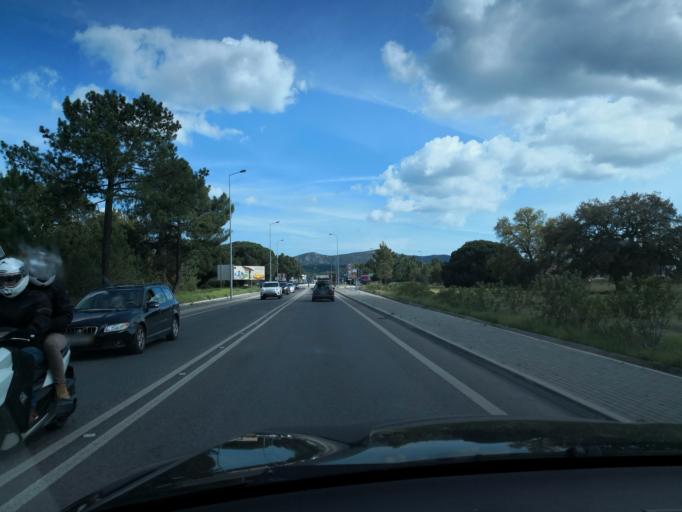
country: PT
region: Setubal
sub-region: Palmela
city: Quinta do Anjo
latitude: 38.5340
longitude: -9.0229
